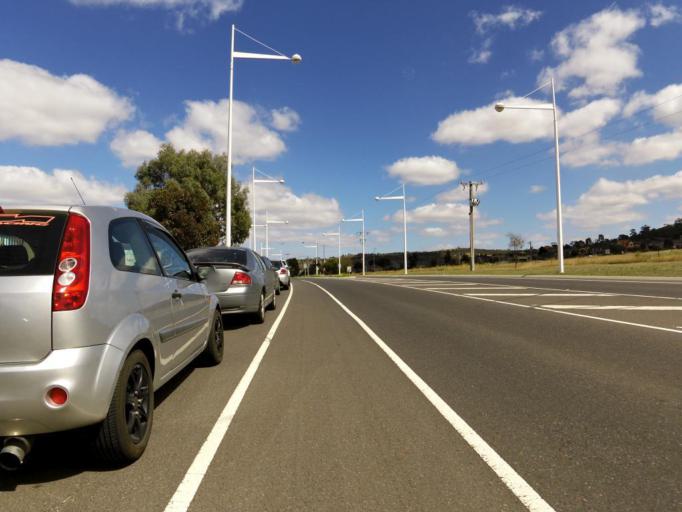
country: AU
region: Victoria
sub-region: Whittlesea
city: Mernda
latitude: -37.6292
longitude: 145.0807
